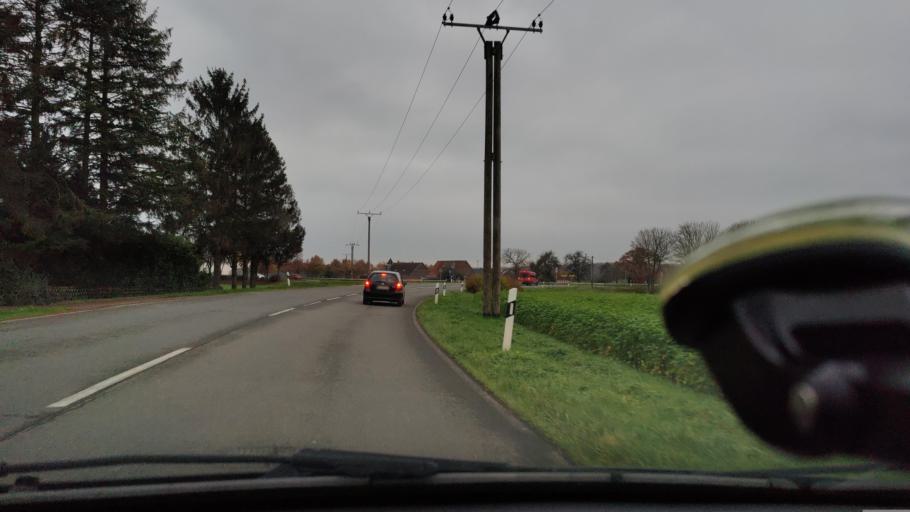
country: DE
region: North Rhine-Westphalia
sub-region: Regierungsbezirk Dusseldorf
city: Kamp-Lintfort
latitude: 51.5434
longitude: 6.5359
